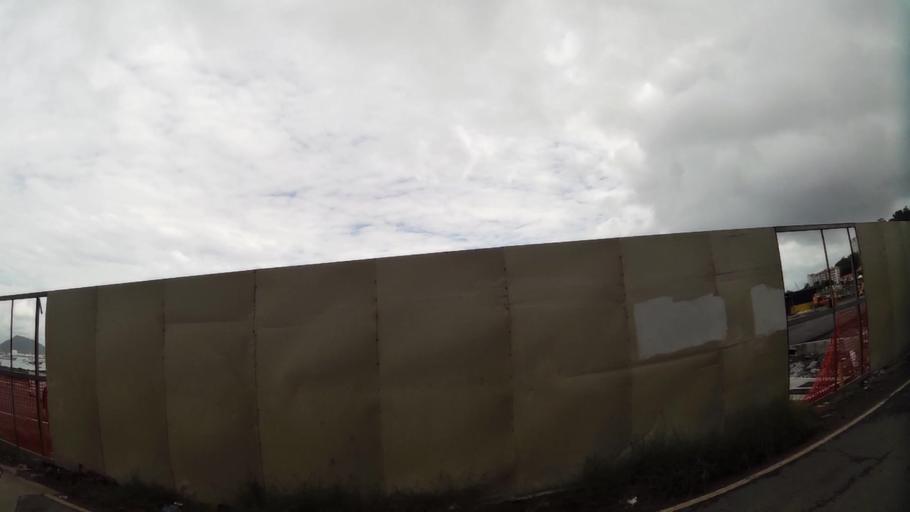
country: PA
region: Panama
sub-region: Distrito de Panama
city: Ancon
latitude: 8.9152
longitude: -79.5306
